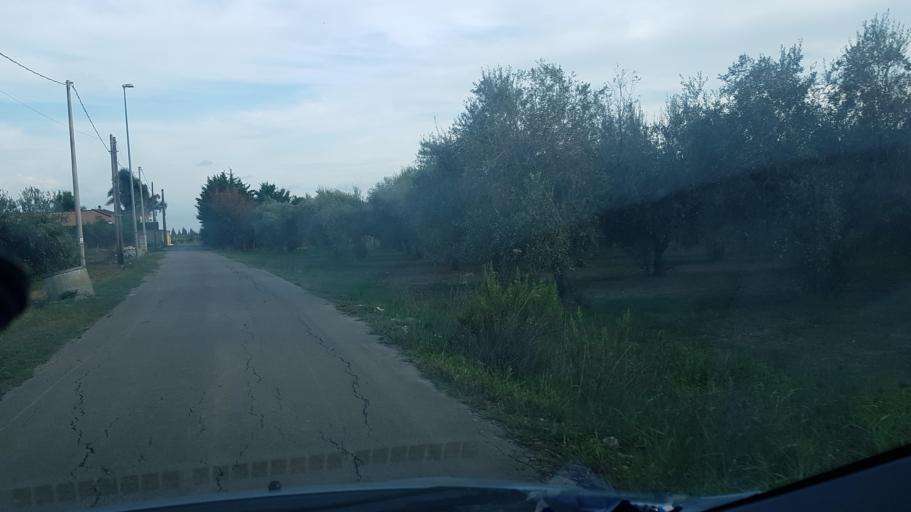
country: IT
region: Apulia
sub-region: Provincia di Lecce
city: Veglie
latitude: 40.3317
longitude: 17.9757
